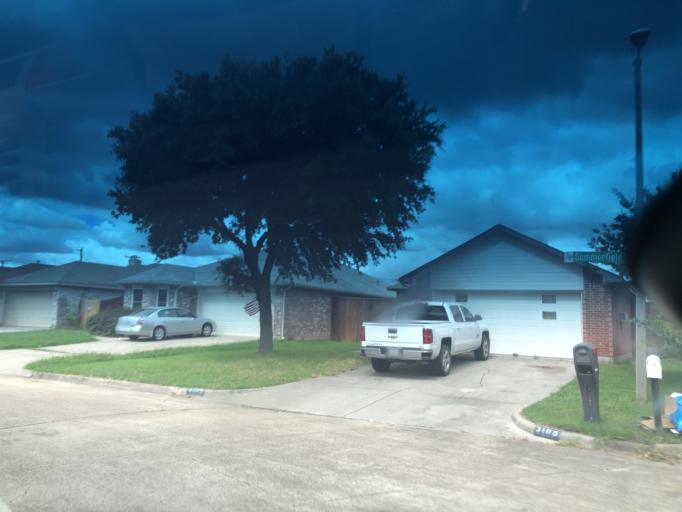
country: US
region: Texas
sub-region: Dallas County
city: Grand Prairie
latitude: 32.6978
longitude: -97.0220
